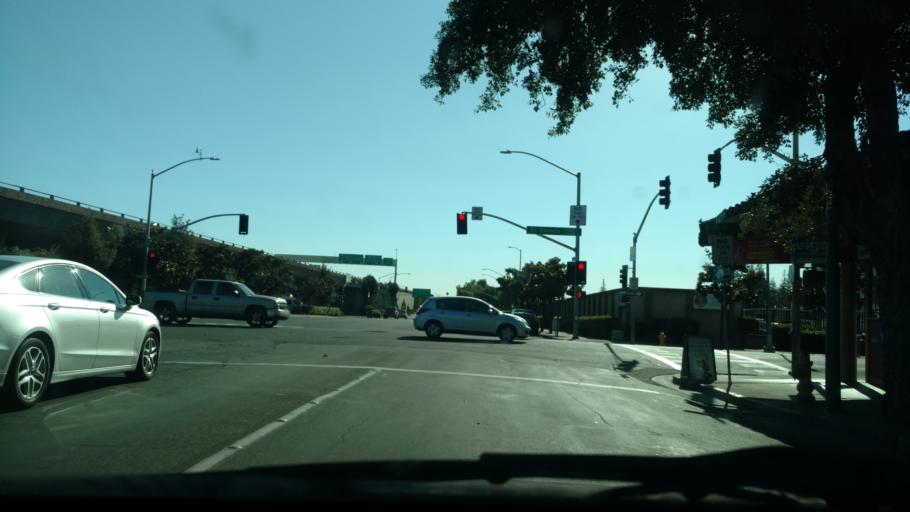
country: US
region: California
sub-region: San Joaquin County
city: Stockton
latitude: 37.9508
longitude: -121.2889
